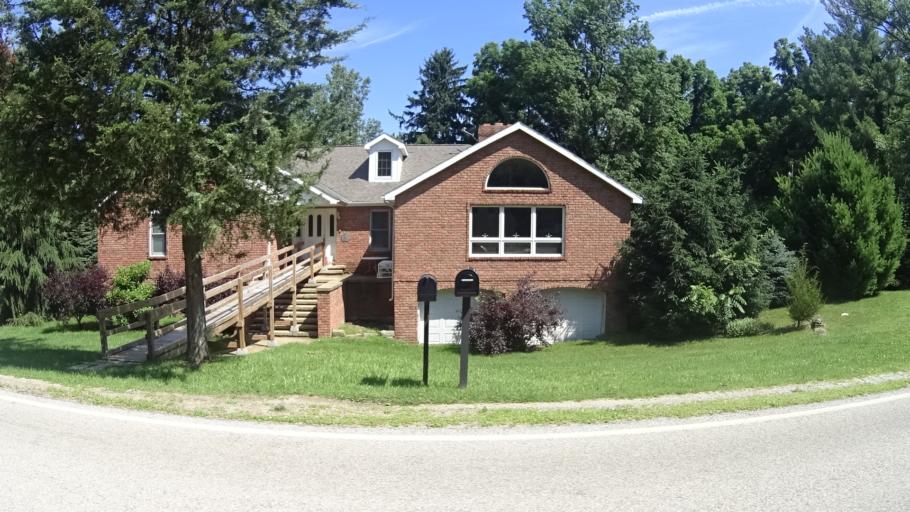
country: US
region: Ohio
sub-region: Erie County
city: Huron
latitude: 41.3323
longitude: -82.4882
